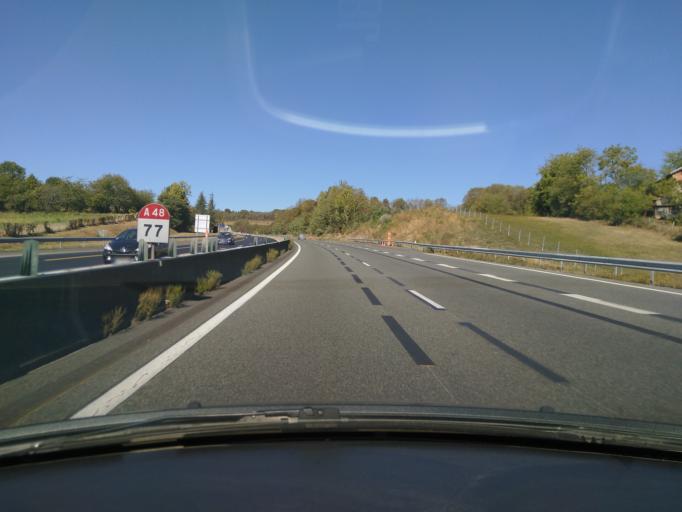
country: FR
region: Rhone-Alpes
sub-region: Departement de l'Isere
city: Saint-Jean-de-Moirans
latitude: 45.3402
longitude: 5.5751
